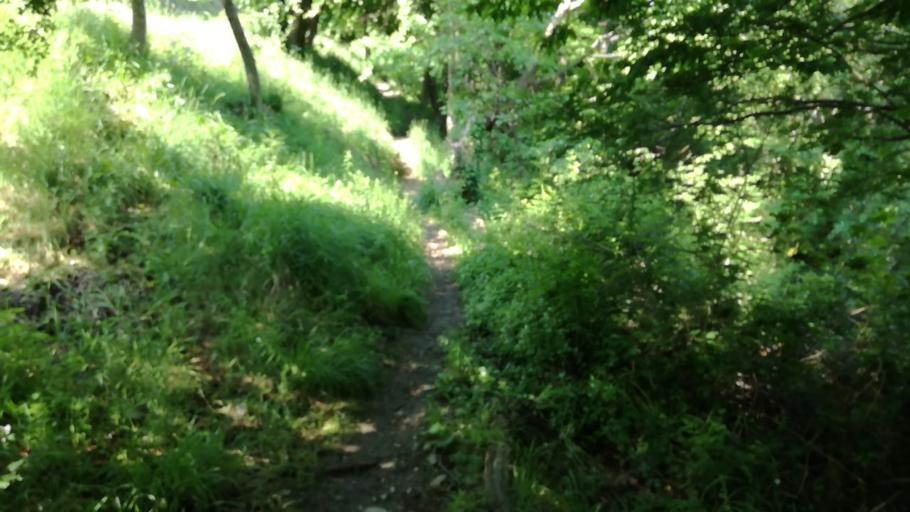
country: IT
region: Liguria
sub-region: Provincia di Genova
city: San Teodoro
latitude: 44.4250
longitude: 8.8999
